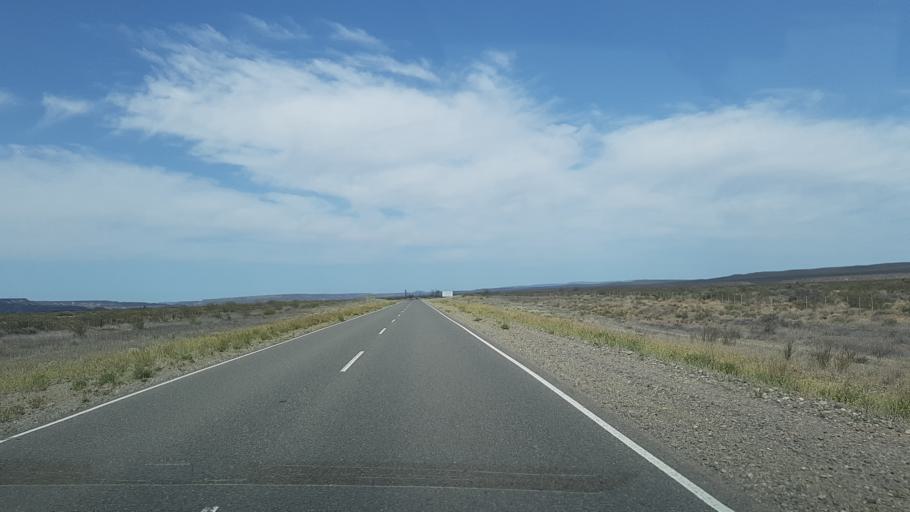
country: AR
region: Neuquen
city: Piedra del Aguila
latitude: -39.8699
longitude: -69.8375
